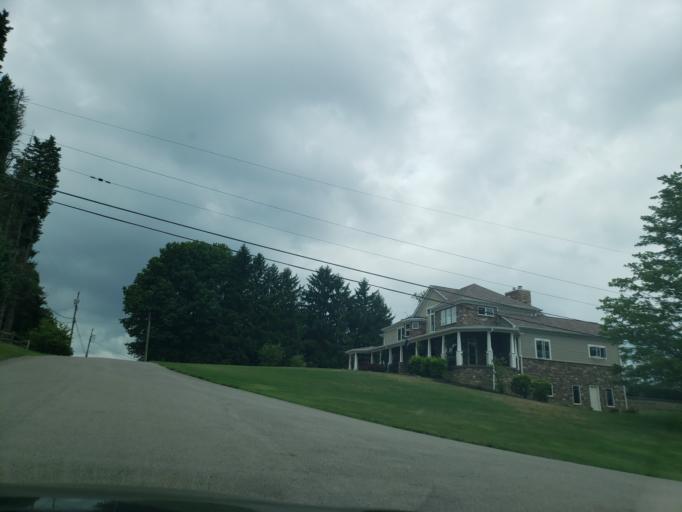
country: US
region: Pennsylvania
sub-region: Allegheny County
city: Coraopolis
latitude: 40.5409
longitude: -80.1610
